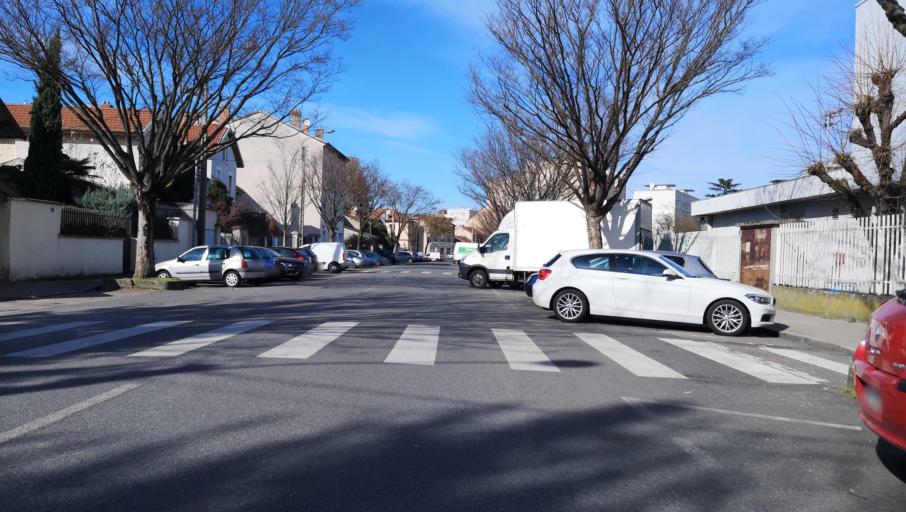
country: FR
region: Rhone-Alpes
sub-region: Departement du Rhone
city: Villeurbanne
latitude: 45.7616
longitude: 4.9006
